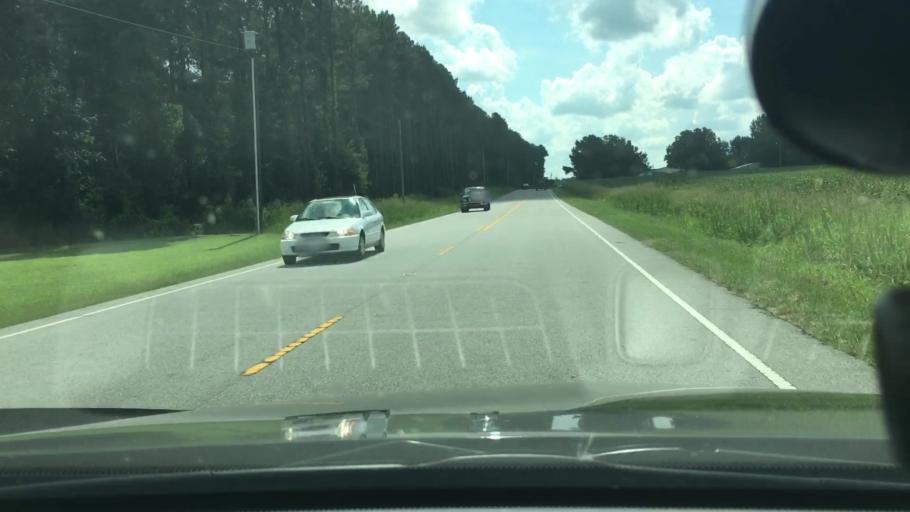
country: US
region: North Carolina
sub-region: Edgecombe County
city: Pinetops
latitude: 35.7163
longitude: -77.5259
